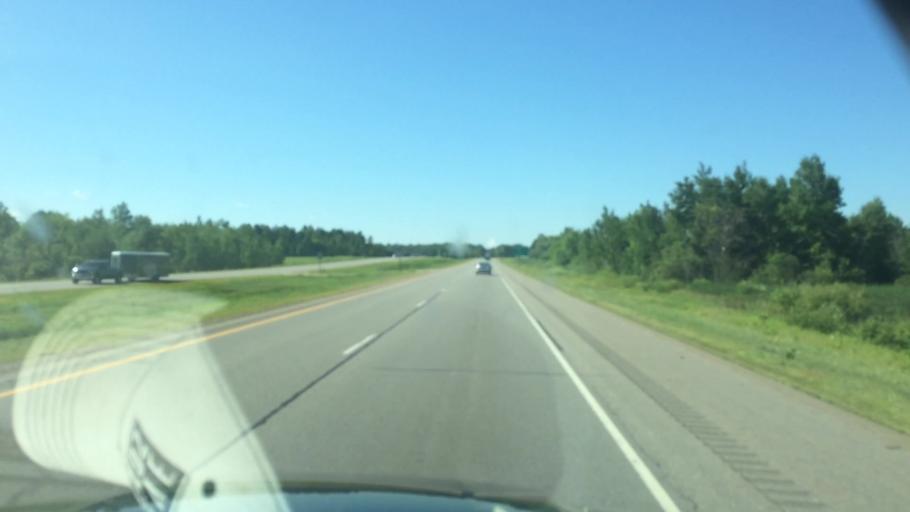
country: US
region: Wisconsin
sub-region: Marathon County
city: Mosinee
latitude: 44.7381
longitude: -89.6800
